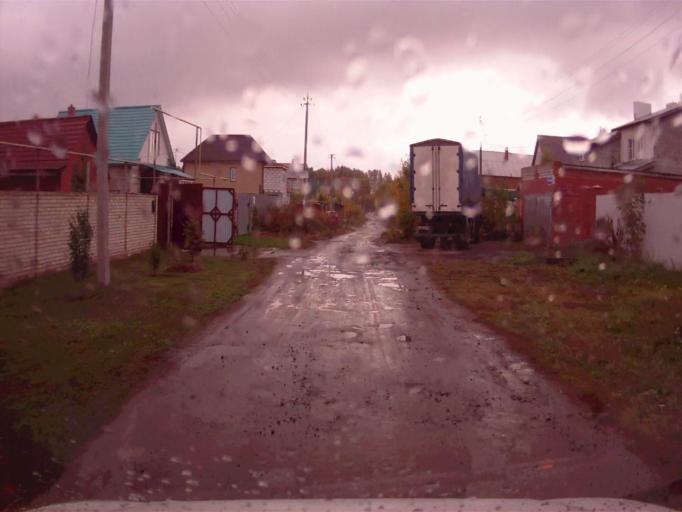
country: RU
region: Chelyabinsk
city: Dolgoderevenskoye
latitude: 55.3044
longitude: 61.3396
